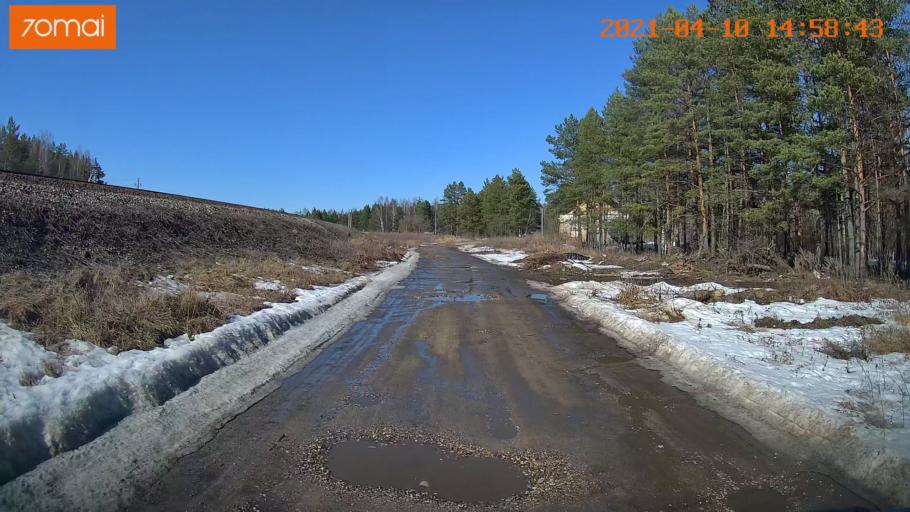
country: RU
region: Ivanovo
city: Kokhma
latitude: 56.9959
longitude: 41.0598
